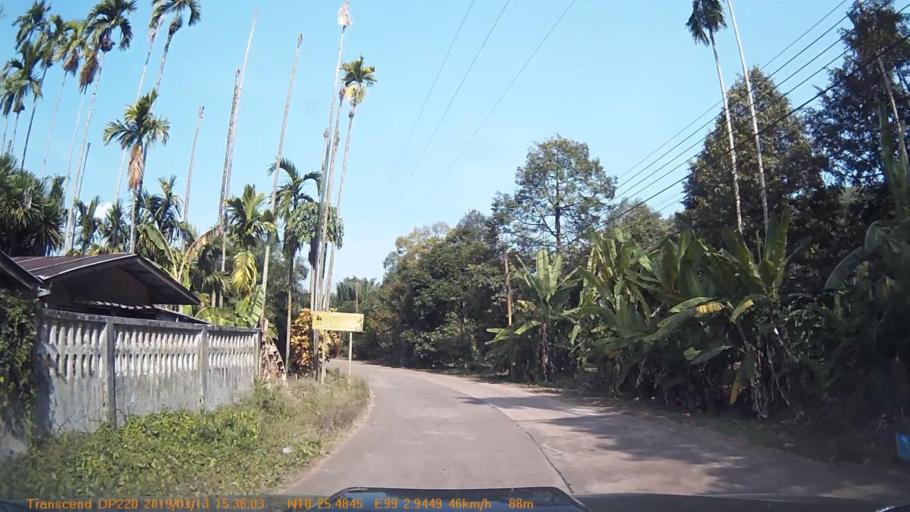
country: TH
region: Chumphon
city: Chumphon
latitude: 10.4247
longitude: 99.0494
